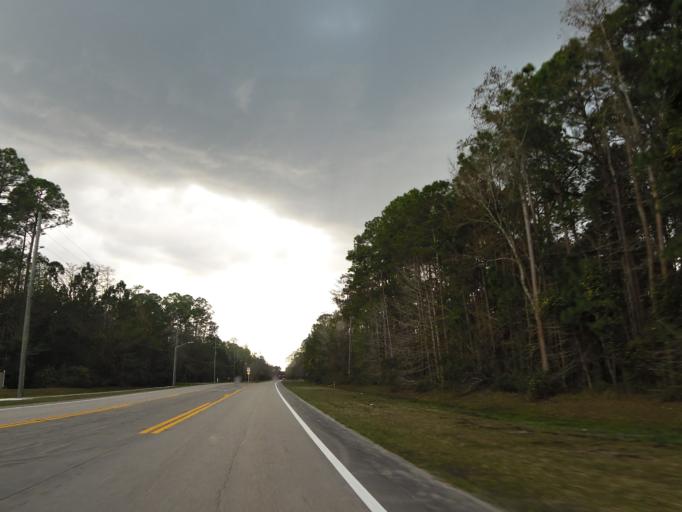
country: US
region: Florida
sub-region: Saint Johns County
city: Fruit Cove
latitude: 30.1865
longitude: -81.5764
